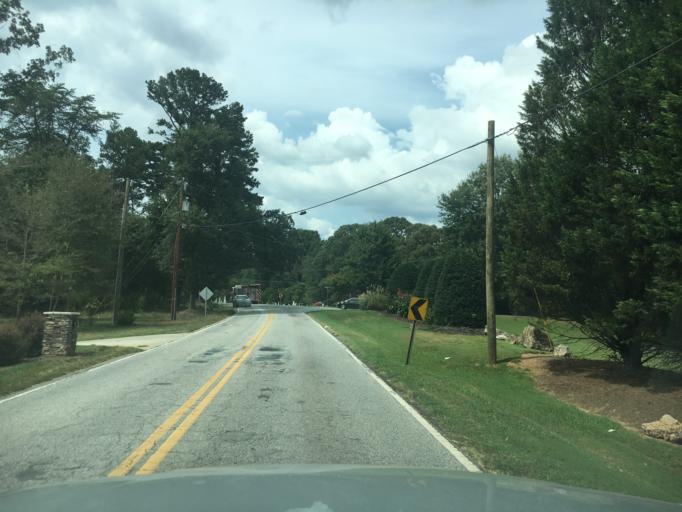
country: US
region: South Carolina
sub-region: Greenville County
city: Five Forks
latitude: 34.8472
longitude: -82.2256
